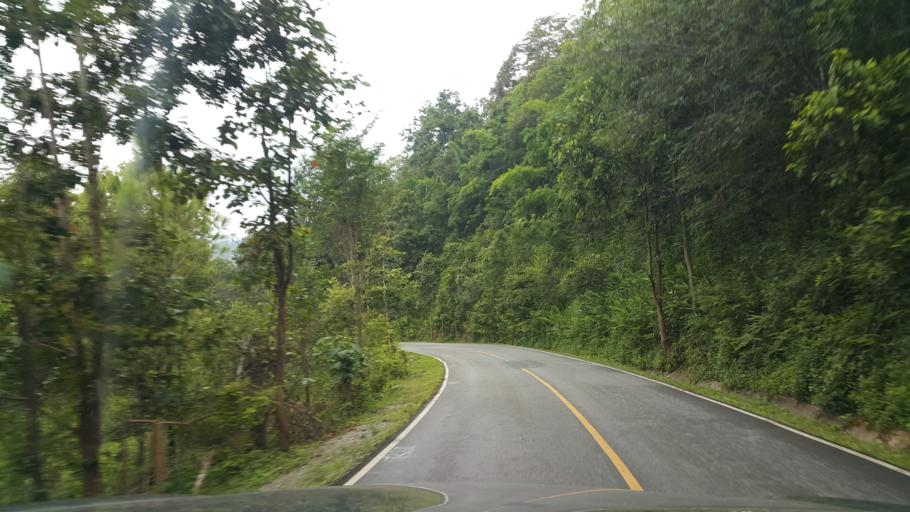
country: TH
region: Chiang Mai
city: Samoeng
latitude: 18.8584
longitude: 98.6576
